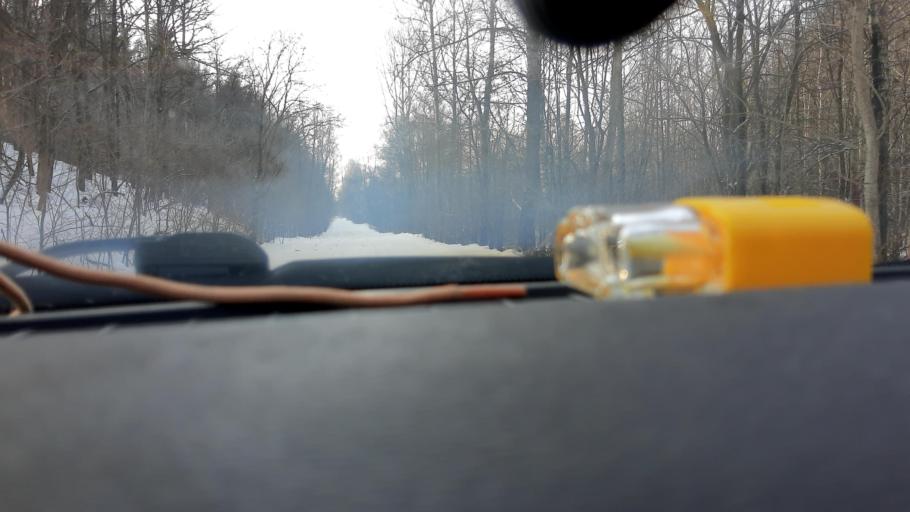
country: RU
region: Bashkortostan
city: Kabakovo
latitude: 54.6329
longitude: 56.0583
